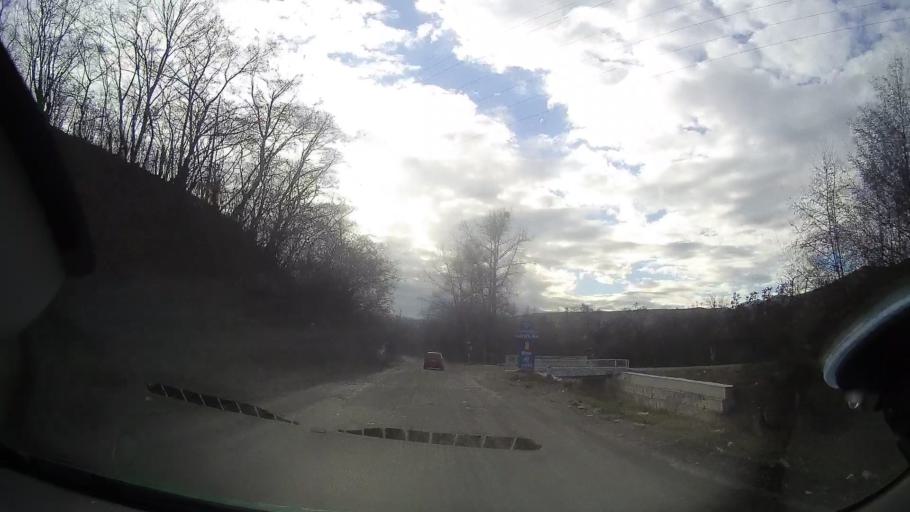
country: RO
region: Cluj
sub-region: Comuna Baisoara
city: Baisoara
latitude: 46.5823
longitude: 23.4627
